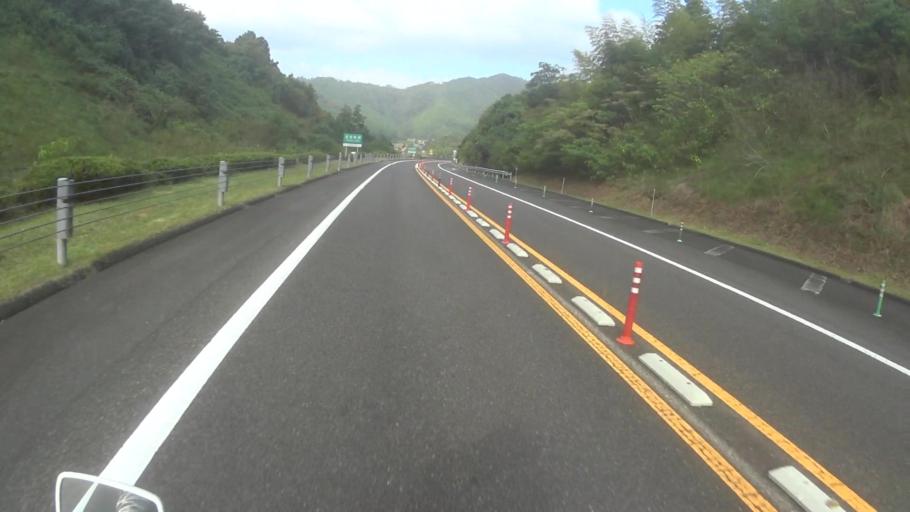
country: JP
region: Kyoto
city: Ayabe
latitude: 35.3831
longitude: 135.2480
